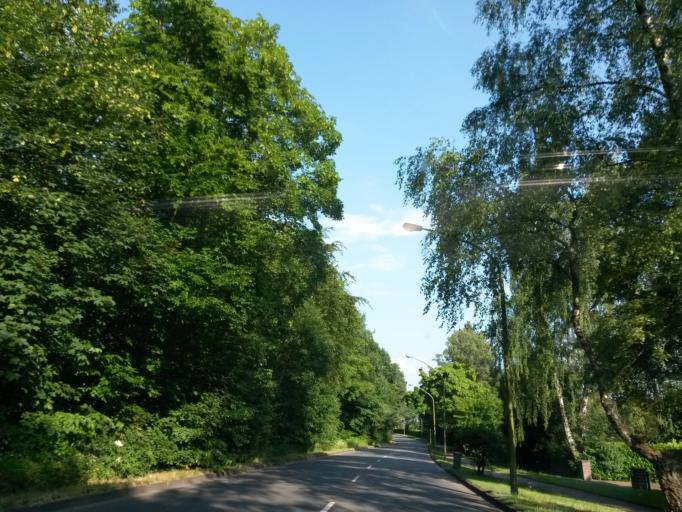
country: DE
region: North Rhine-Westphalia
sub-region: Regierungsbezirk Dusseldorf
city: Dinslaken
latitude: 51.5610
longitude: 6.8217
